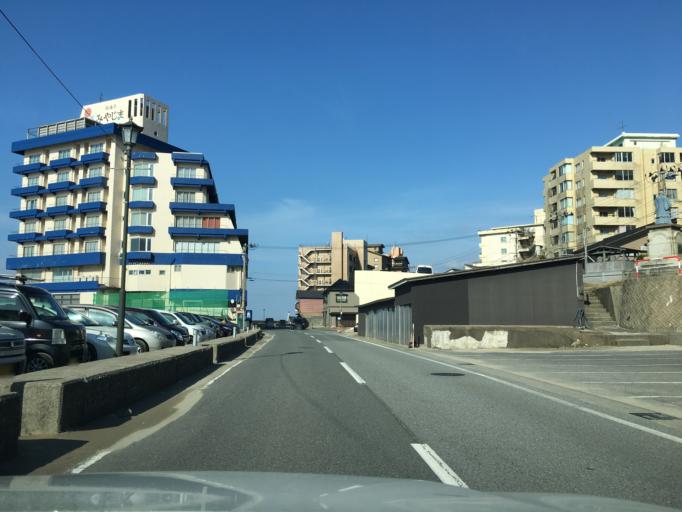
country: JP
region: Yamagata
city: Tsuruoka
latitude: 38.7771
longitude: 139.7491
